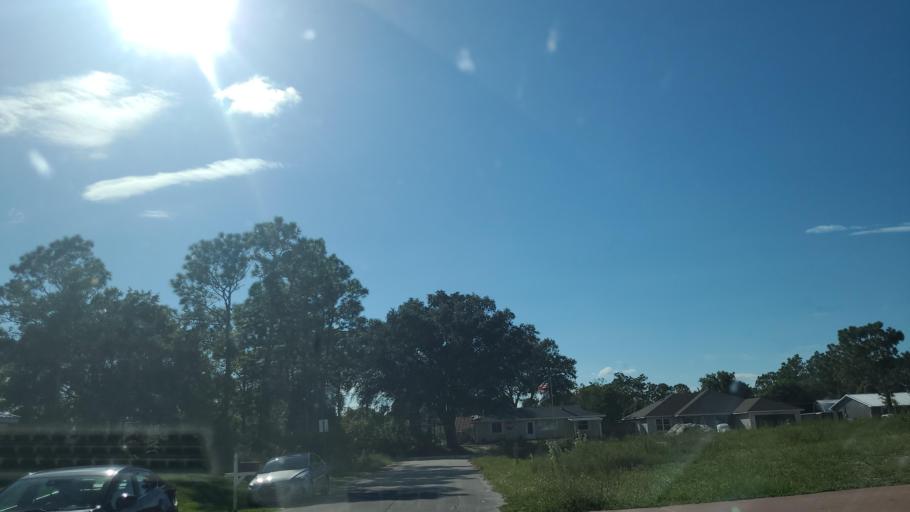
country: US
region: Florida
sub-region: Brevard County
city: Grant-Valkaria
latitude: 27.9645
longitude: -80.6254
